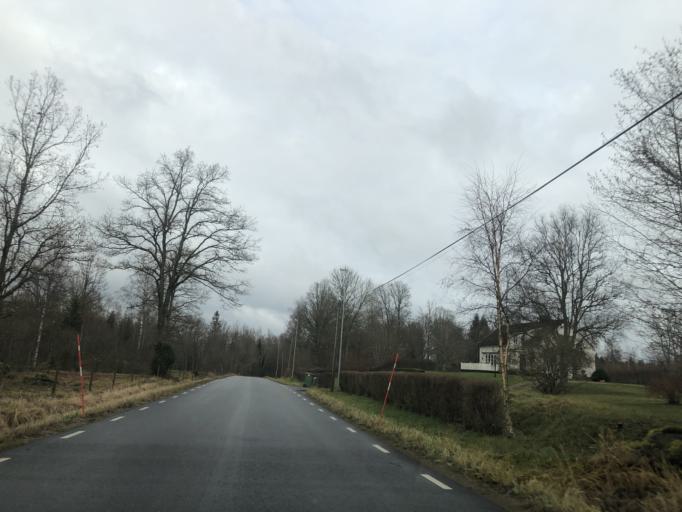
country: SE
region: Vaestra Goetaland
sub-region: Ulricehamns Kommun
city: Ulricehamn
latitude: 57.8310
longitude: 13.2576
